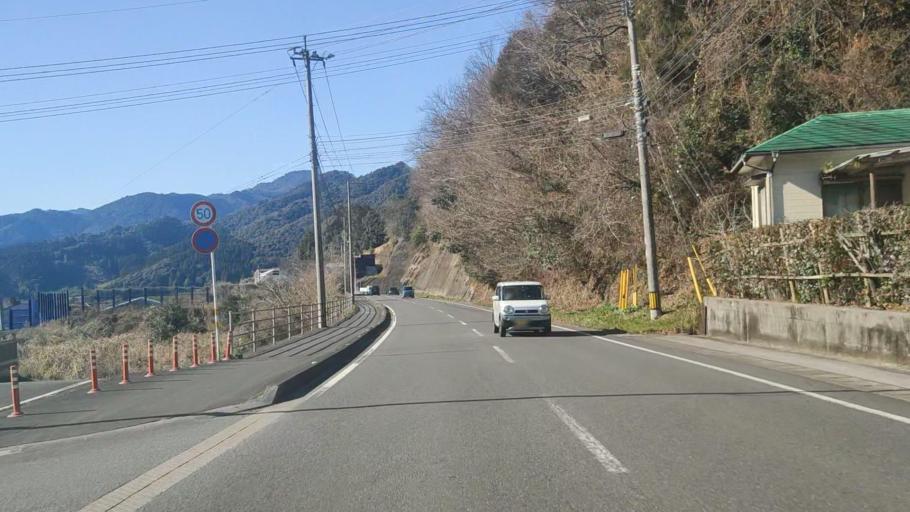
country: JP
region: Oita
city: Saiki
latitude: 32.9755
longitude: 131.8560
